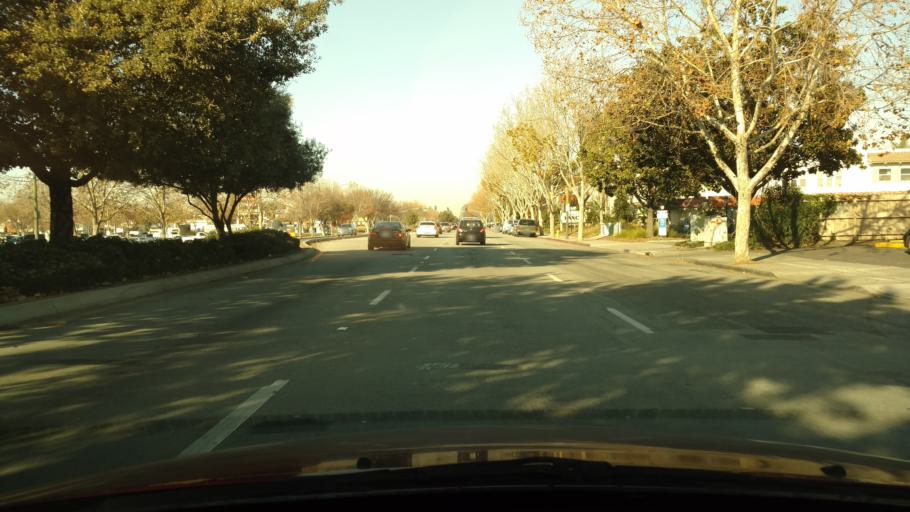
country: US
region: California
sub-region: Santa Clara County
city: Campbell
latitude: 37.2994
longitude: -121.9498
